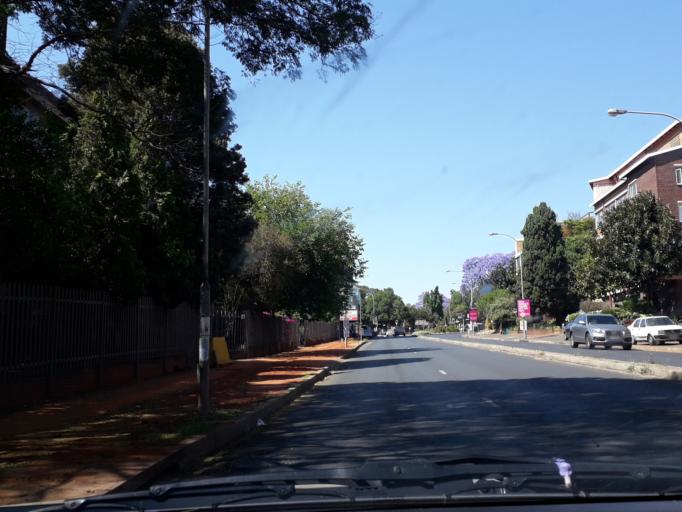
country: ZA
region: Gauteng
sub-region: City of Johannesburg Metropolitan Municipality
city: Johannesburg
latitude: -26.1336
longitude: 28.0485
